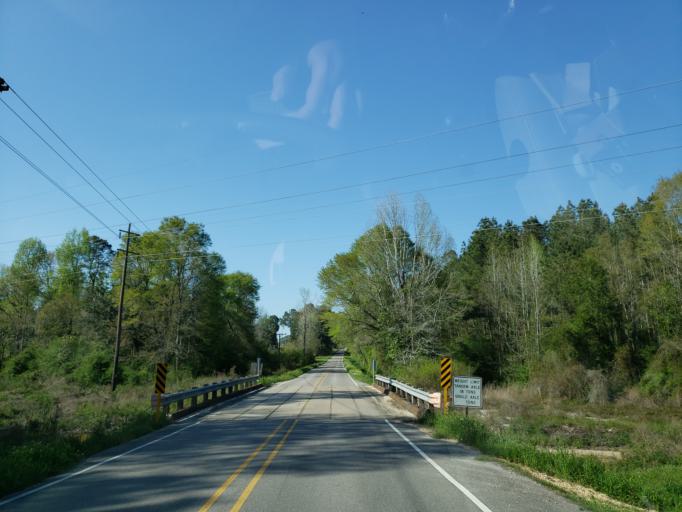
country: US
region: Mississippi
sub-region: Forrest County
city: Rawls Springs
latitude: 31.5505
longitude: -89.3657
